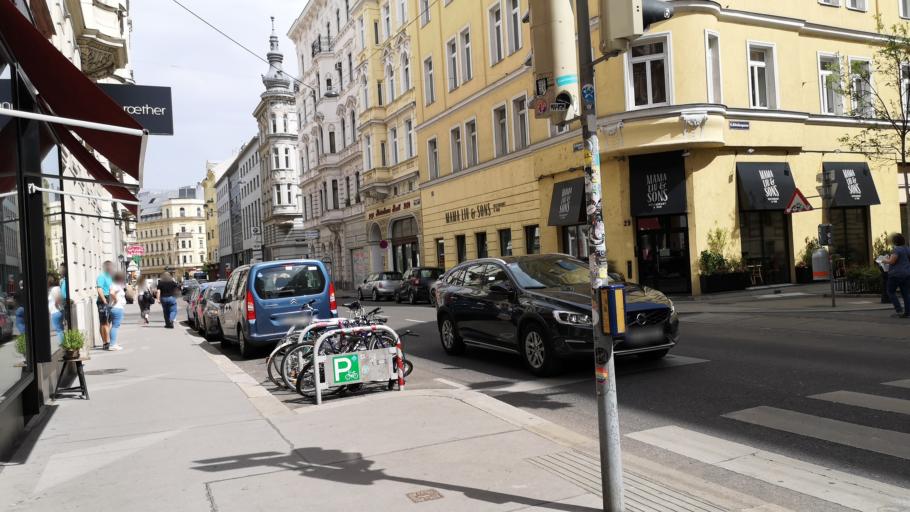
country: AT
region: Vienna
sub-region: Wien Stadt
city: Vienna
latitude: 48.1989
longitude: 16.3585
